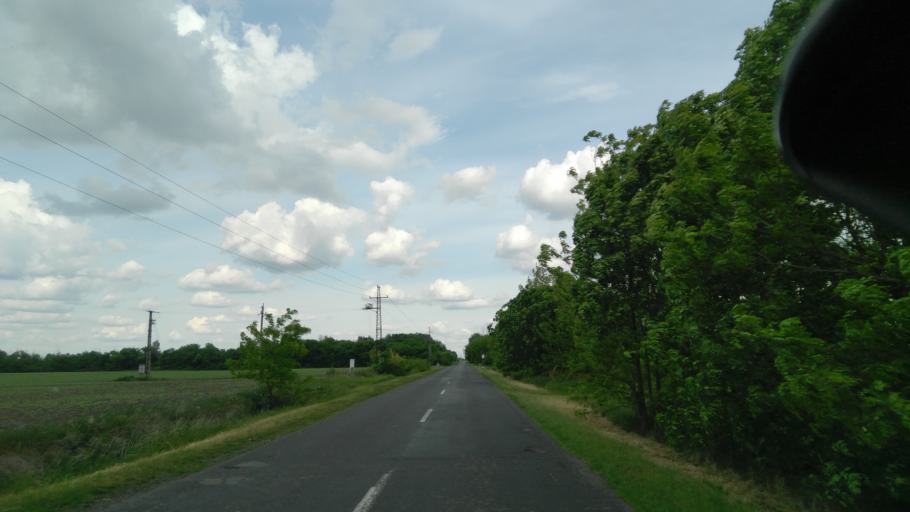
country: HU
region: Bekes
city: Battonya
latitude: 46.2948
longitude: 20.9716
